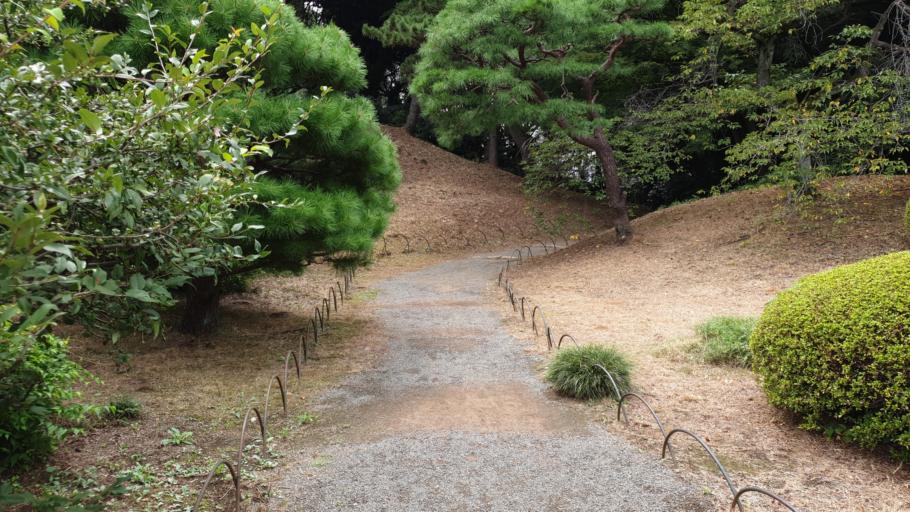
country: JP
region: Tokyo
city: Tokyo
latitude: 35.6851
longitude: 139.7059
